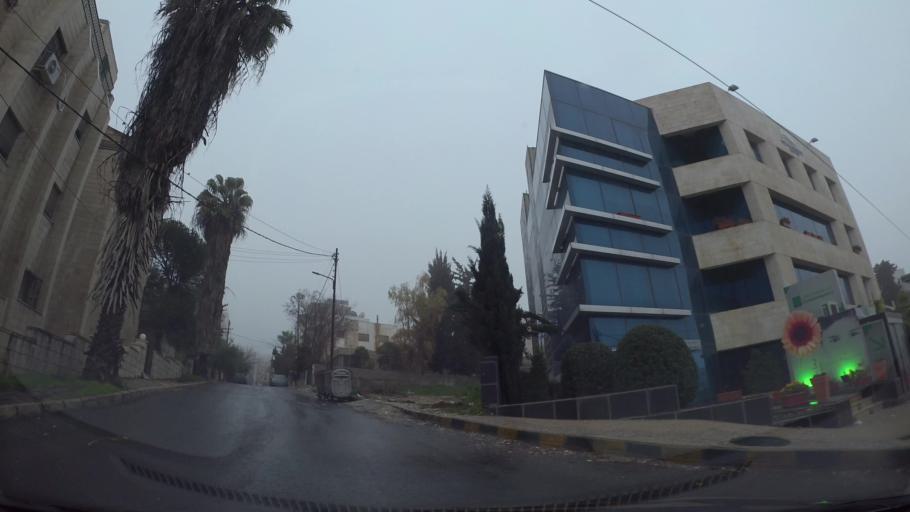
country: JO
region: Amman
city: Wadi as Sir
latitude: 31.9632
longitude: 35.8780
